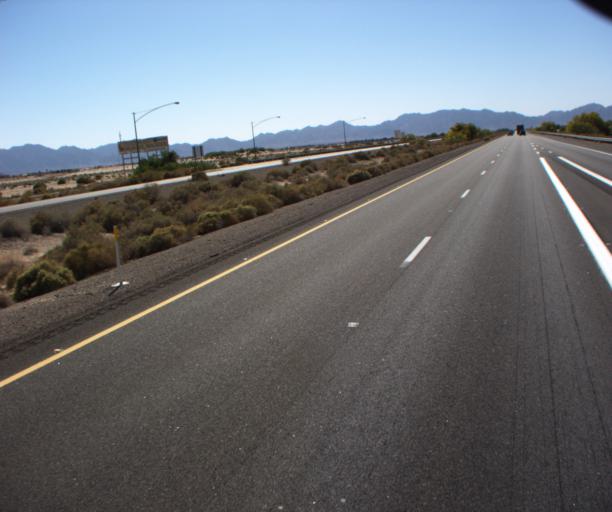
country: US
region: Arizona
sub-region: Yuma County
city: Wellton
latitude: 32.6611
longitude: -114.1461
